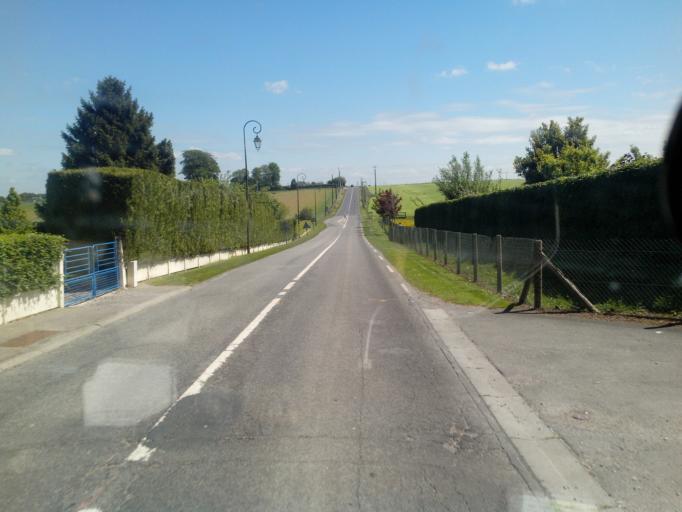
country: FR
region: Haute-Normandie
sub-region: Departement de la Seine-Maritime
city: Turretot
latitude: 49.6186
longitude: 0.2820
